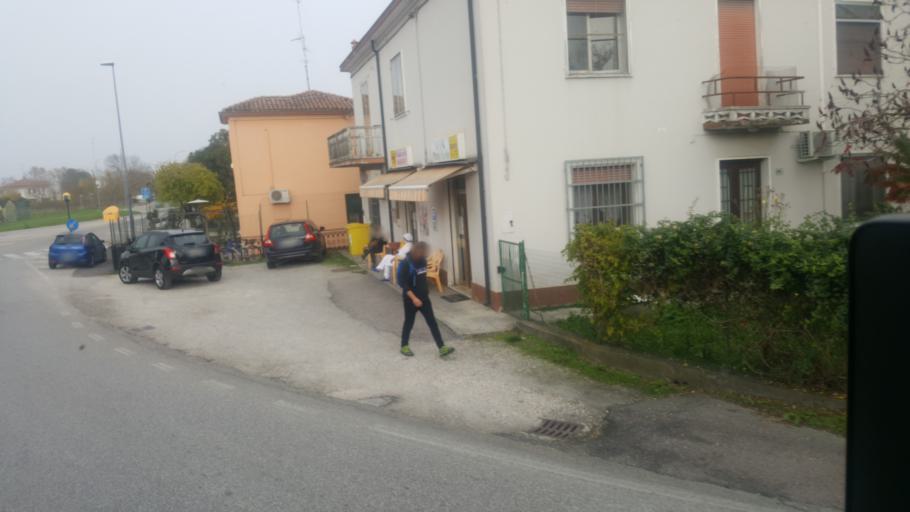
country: IT
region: Emilia-Romagna
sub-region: Provincia di Ferrara
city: Bondeno
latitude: 44.8950
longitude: 11.4050
